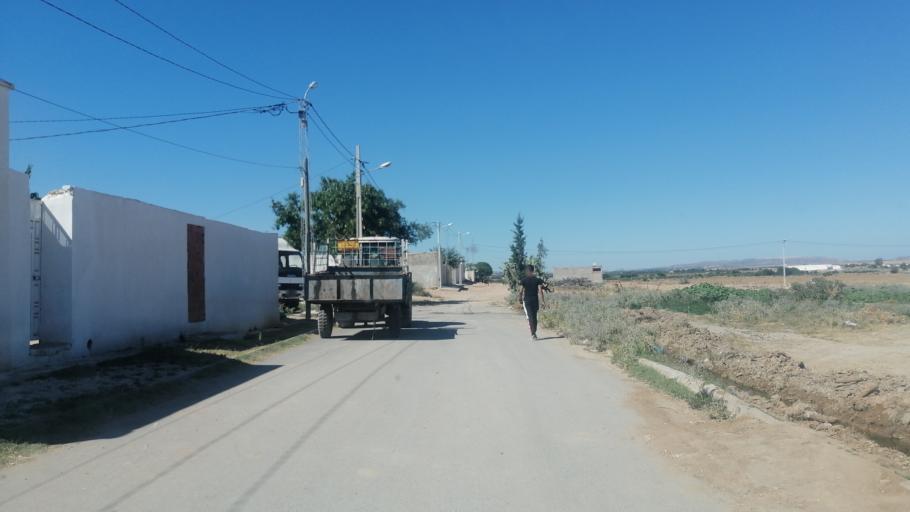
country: TN
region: Al Qayrawan
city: Sbikha
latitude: 36.1263
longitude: 10.0965
